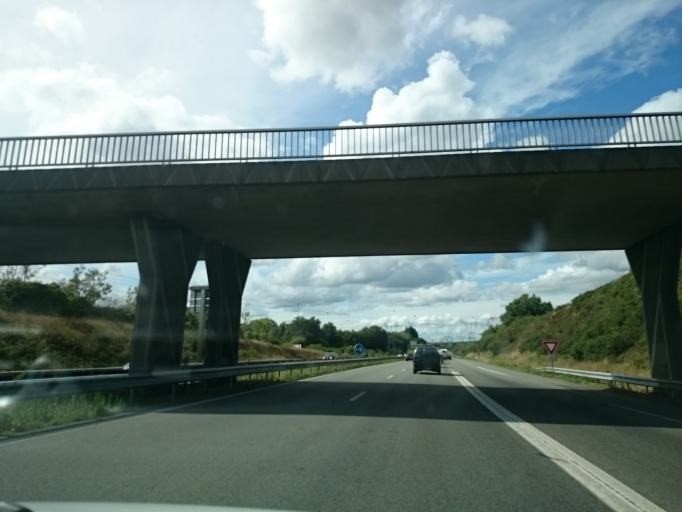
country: FR
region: Pays de la Loire
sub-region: Departement de la Loire-Atlantique
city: Bouguenais
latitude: 47.1728
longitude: -1.5920
